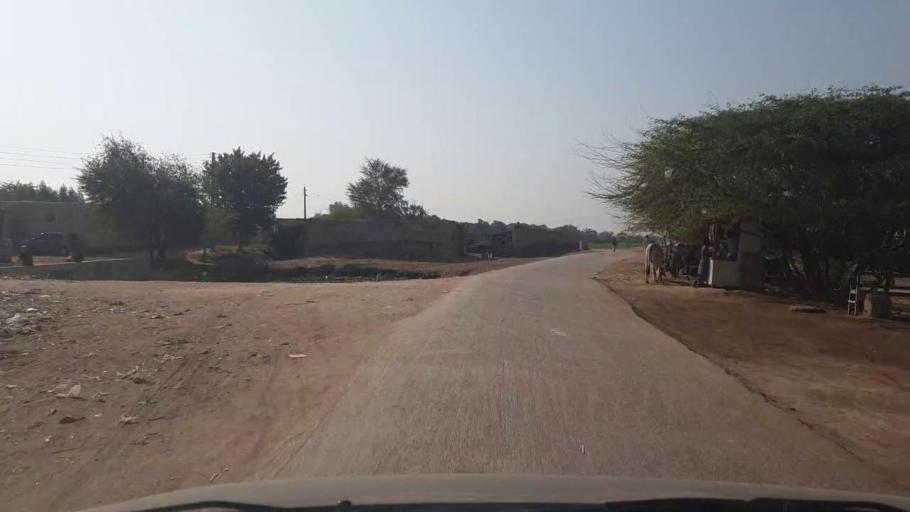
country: PK
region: Sindh
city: Mirwah Gorchani
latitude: 25.3114
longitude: 69.1522
